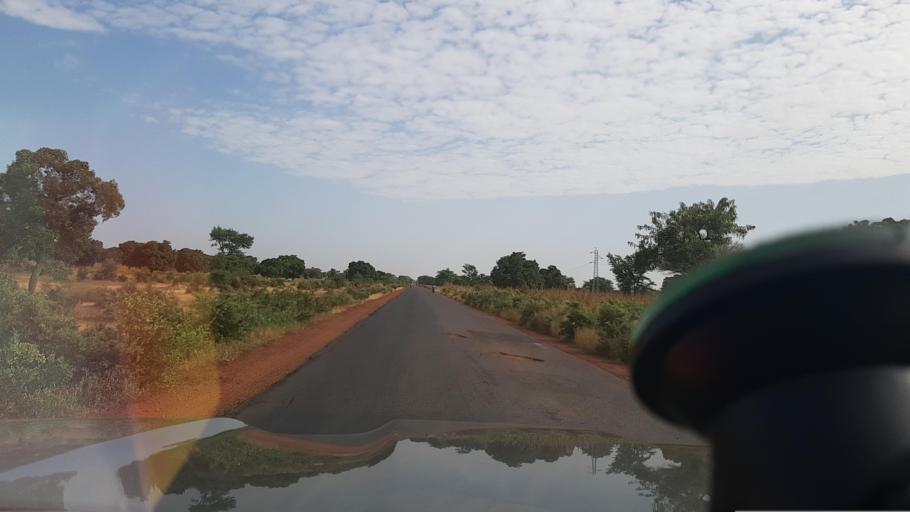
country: ML
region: Segou
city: Segou
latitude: 13.5141
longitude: -6.1401
